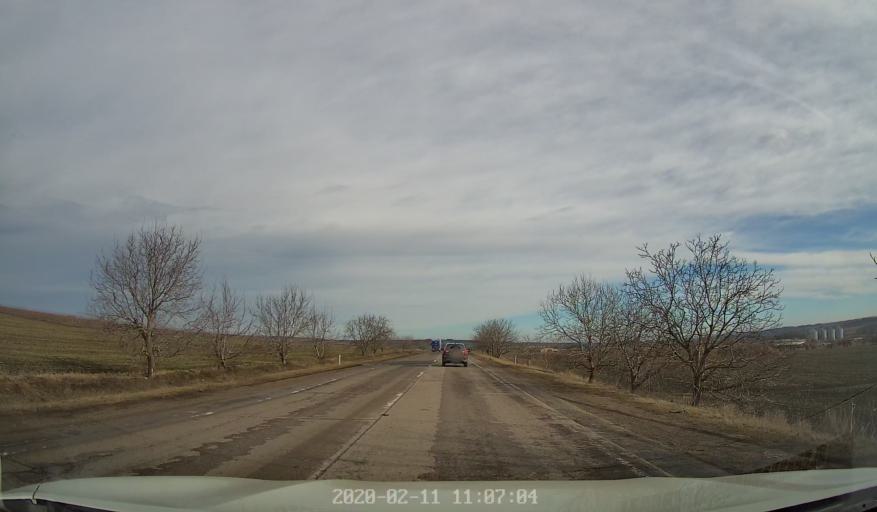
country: MD
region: Balti
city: Balti
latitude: 47.7251
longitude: 27.8150
